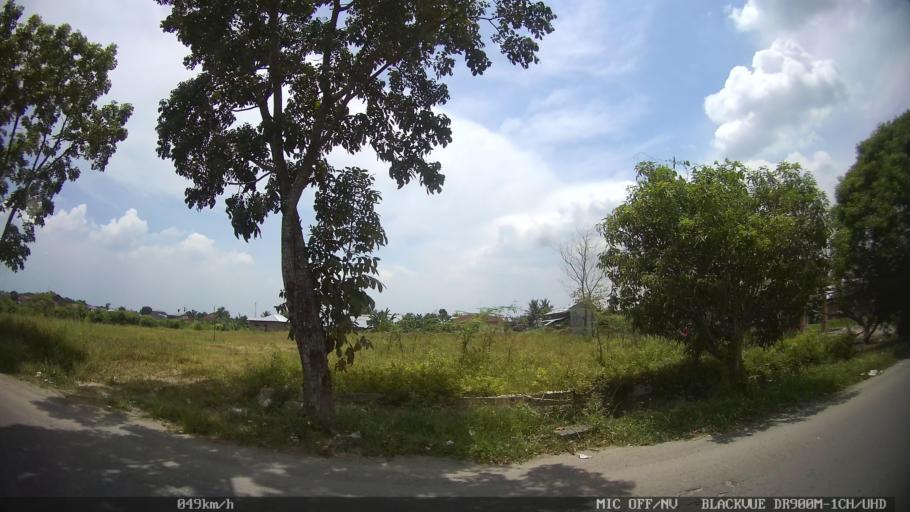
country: ID
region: North Sumatra
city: Binjai
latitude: 3.6243
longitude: 98.5185
